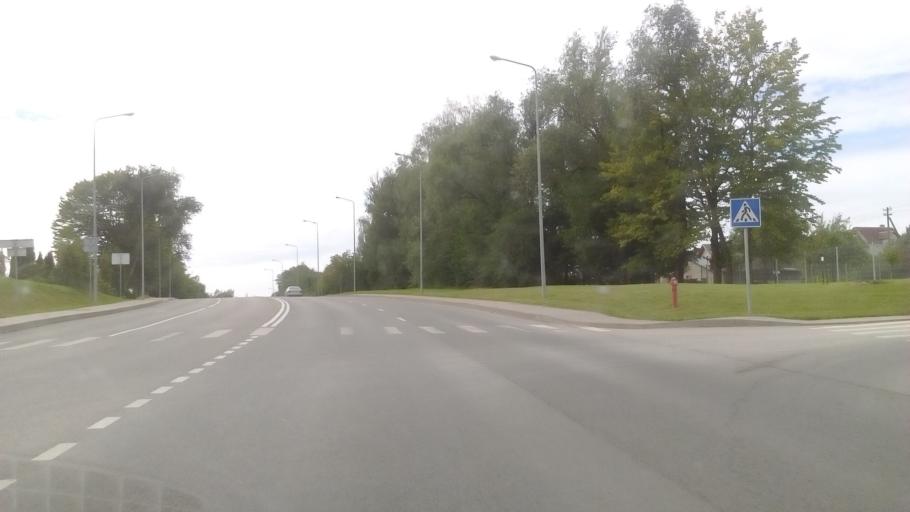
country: LT
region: Alytaus apskritis
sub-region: Alytus
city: Alytus
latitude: 54.3931
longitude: 24.0068
